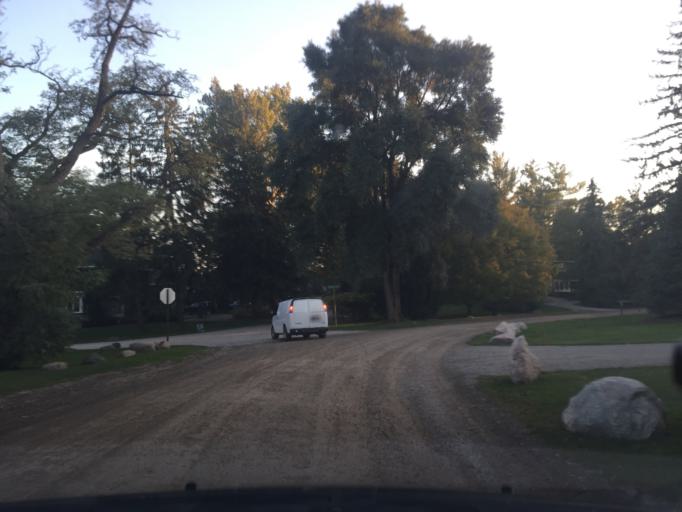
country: US
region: Michigan
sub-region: Oakland County
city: Franklin
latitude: 42.5493
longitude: -83.2936
